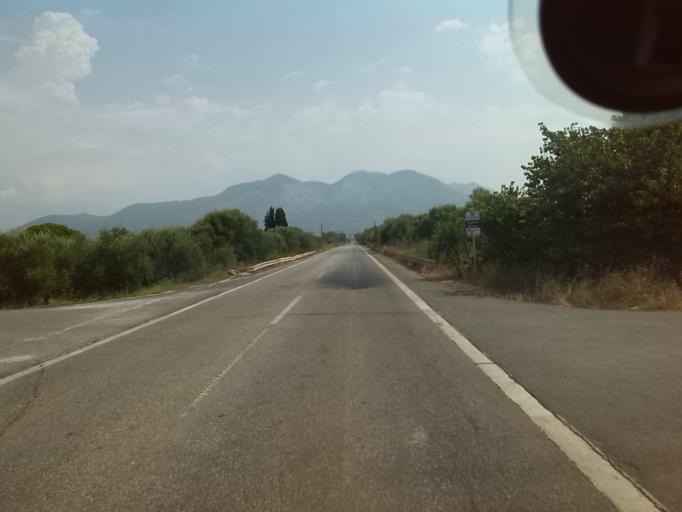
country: GR
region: Peloponnese
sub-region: Nomos Messinias
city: Kyparissia
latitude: 37.3108
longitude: 21.7023
